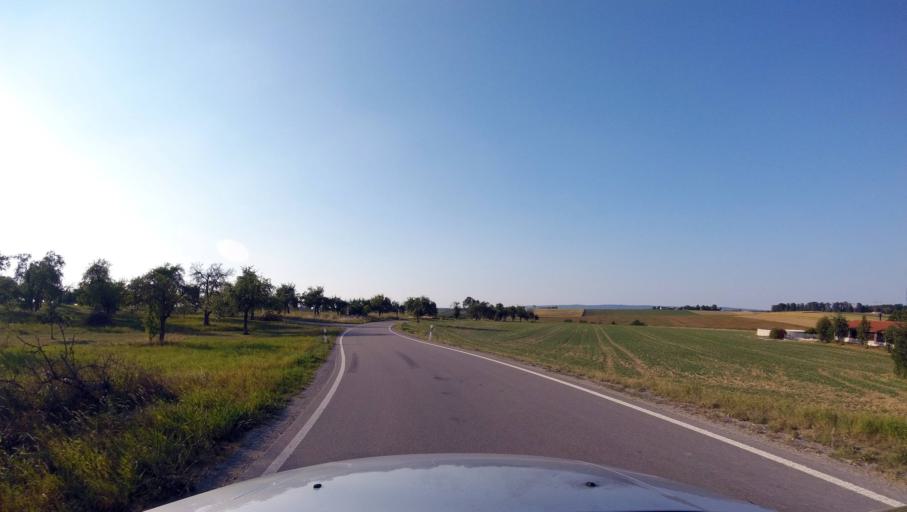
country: DE
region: Baden-Wuerttemberg
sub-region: Regierungsbezirk Stuttgart
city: Leutenbach
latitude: 48.9093
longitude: 9.4018
